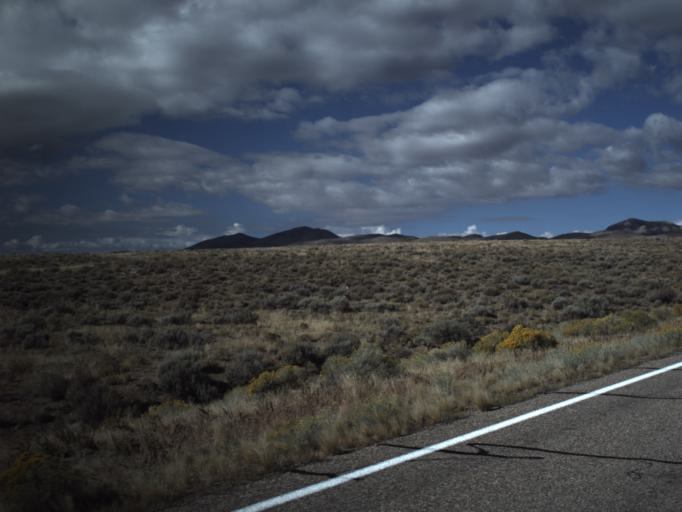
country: US
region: Utah
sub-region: Beaver County
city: Milford
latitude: 38.4457
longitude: -113.1823
